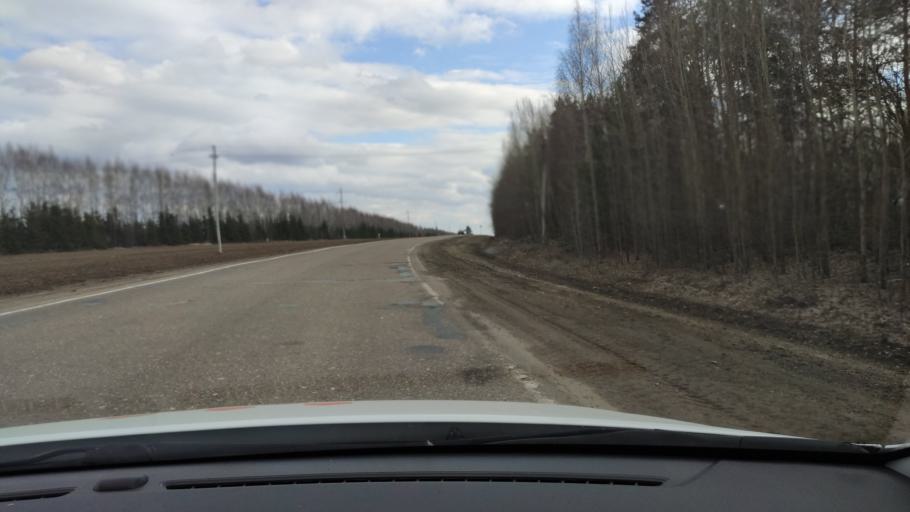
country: RU
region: Tatarstan
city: Vysokaya Gora
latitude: 56.0621
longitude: 49.2040
